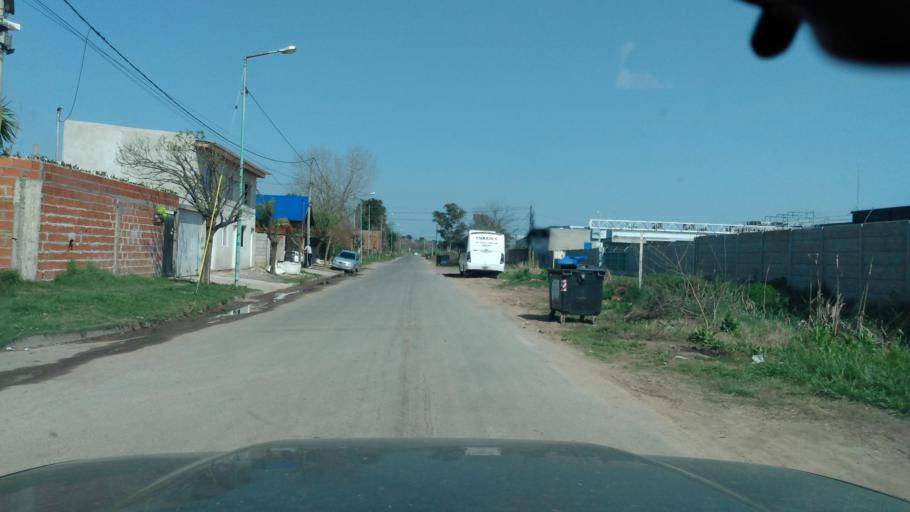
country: AR
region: Buenos Aires
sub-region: Partido de Lujan
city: Lujan
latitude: -34.5472
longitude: -59.1089
